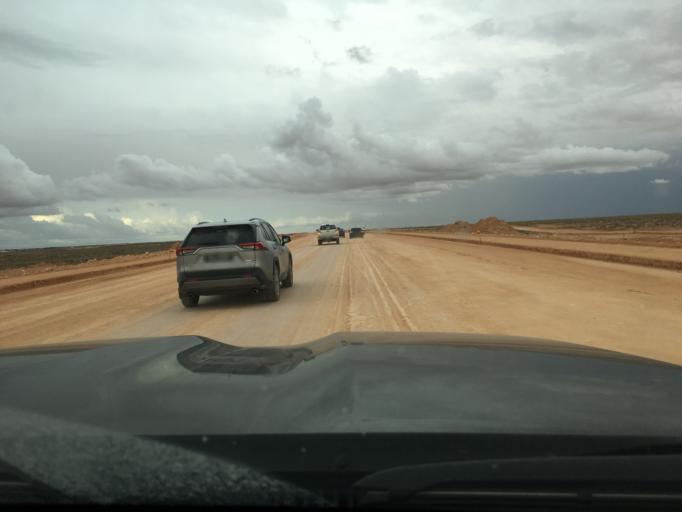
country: TN
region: Madanin
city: Medenine
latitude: 33.2693
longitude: 10.5858
